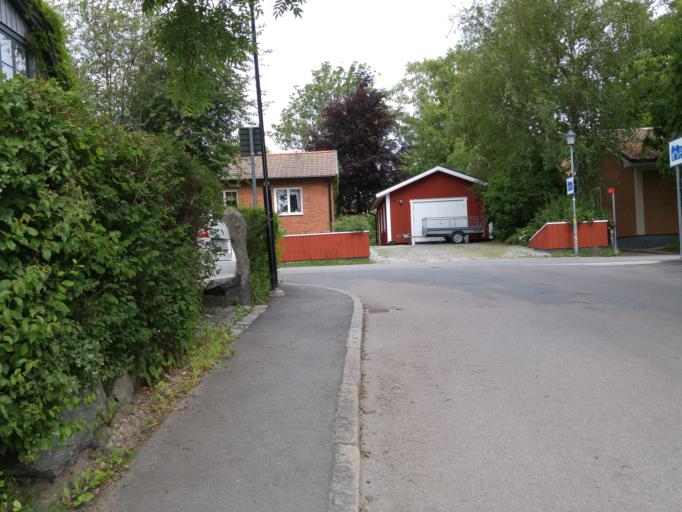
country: SE
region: Stockholm
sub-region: Sigtuna Kommun
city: Sigtuna
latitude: 59.6151
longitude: 17.7161
